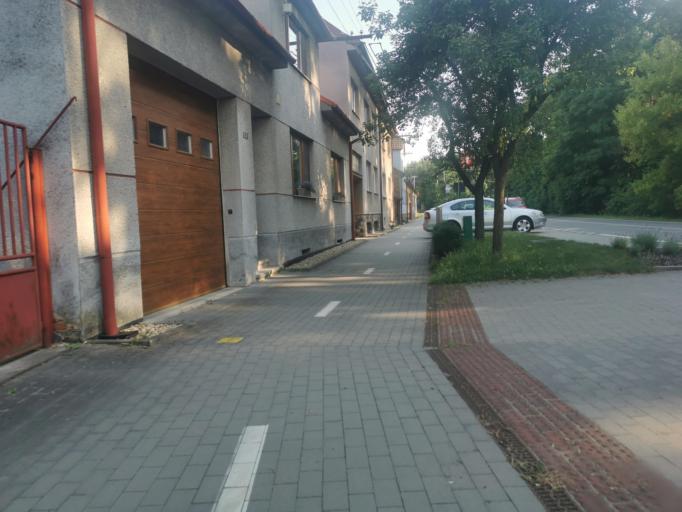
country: CZ
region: South Moravian
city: Ratiskovice
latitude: 48.9150
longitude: 17.1606
